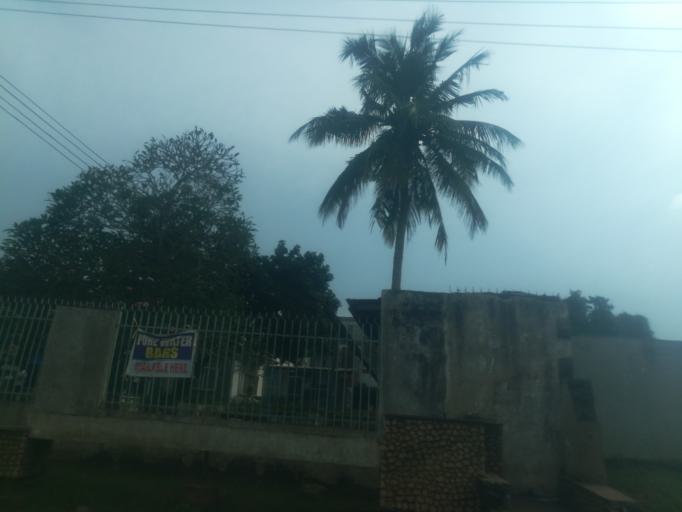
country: NG
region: Ogun
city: Abeokuta
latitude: 7.1361
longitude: 3.3015
